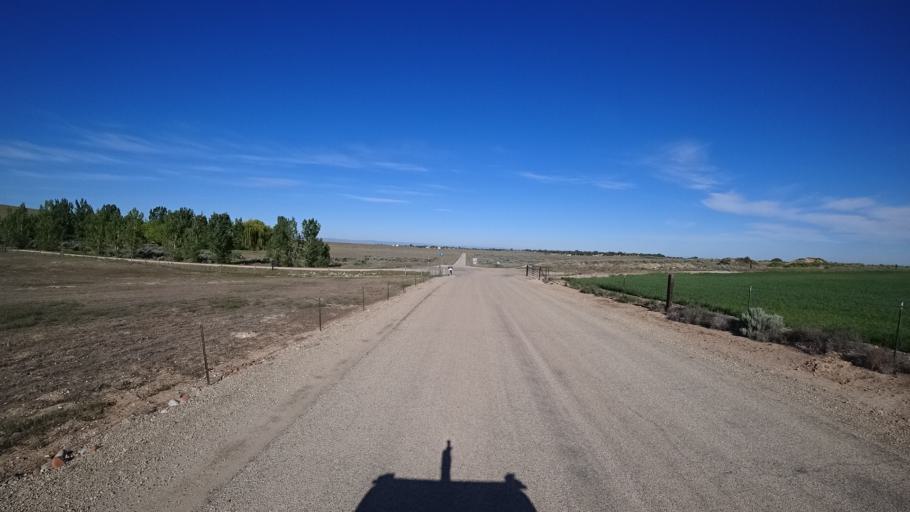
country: US
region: Idaho
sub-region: Ada County
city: Garden City
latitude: 43.5248
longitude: -116.2887
